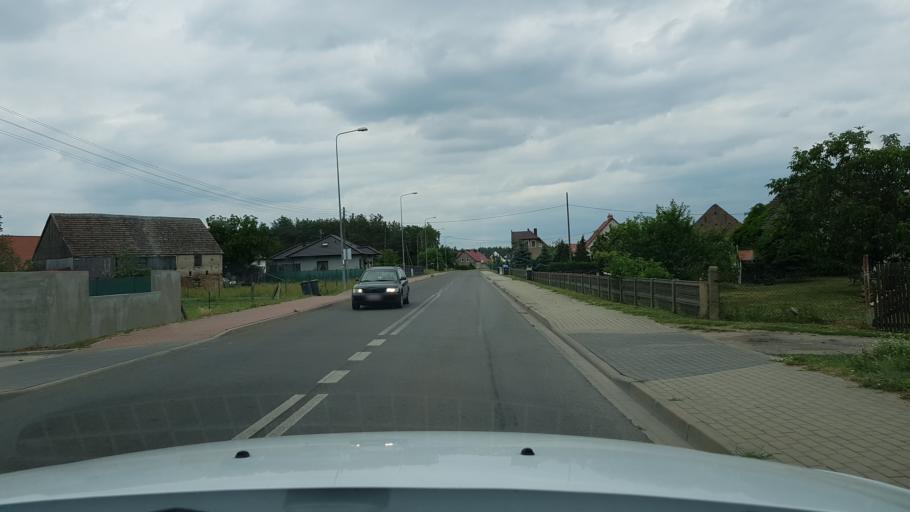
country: PL
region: Lubusz
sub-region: Powiat gorzowski
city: Kostrzyn nad Odra
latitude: 52.6220
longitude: 14.5886
